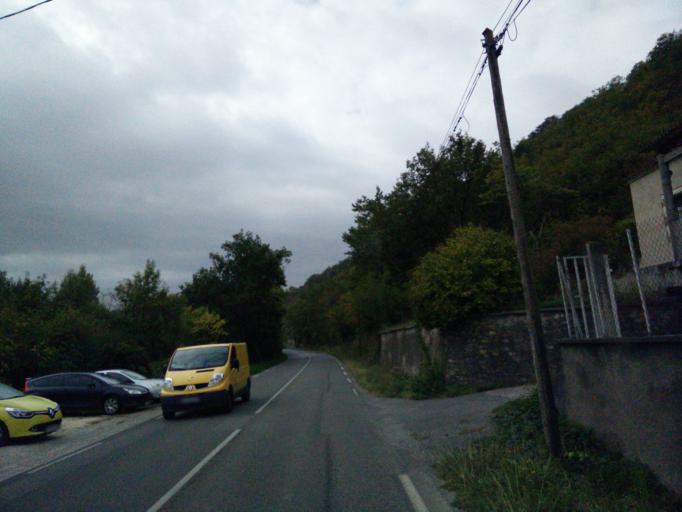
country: FR
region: Midi-Pyrenees
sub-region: Departement du Lot
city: Cahors
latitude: 44.4695
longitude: 1.4453
